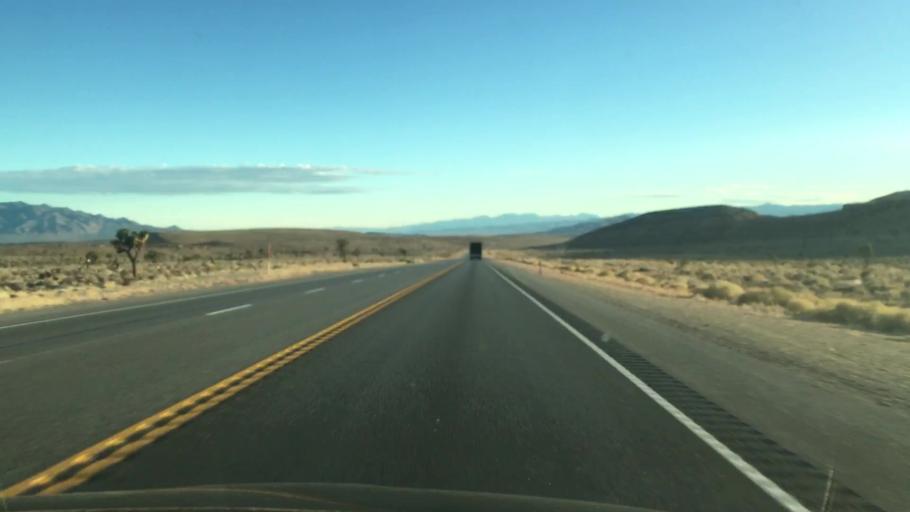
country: US
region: Nevada
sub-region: Esmeralda County
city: Goldfield
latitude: 37.6633
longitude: -117.2180
